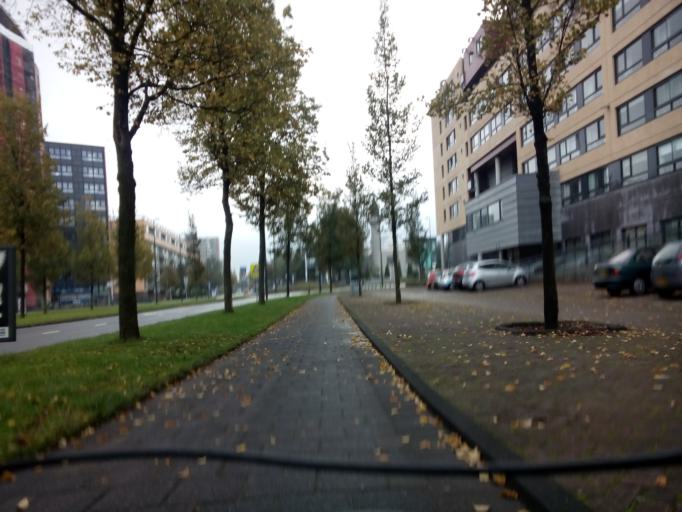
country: NL
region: South Holland
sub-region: Gemeente Maassluis
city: Maassluis
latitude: 51.9276
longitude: 4.2451
